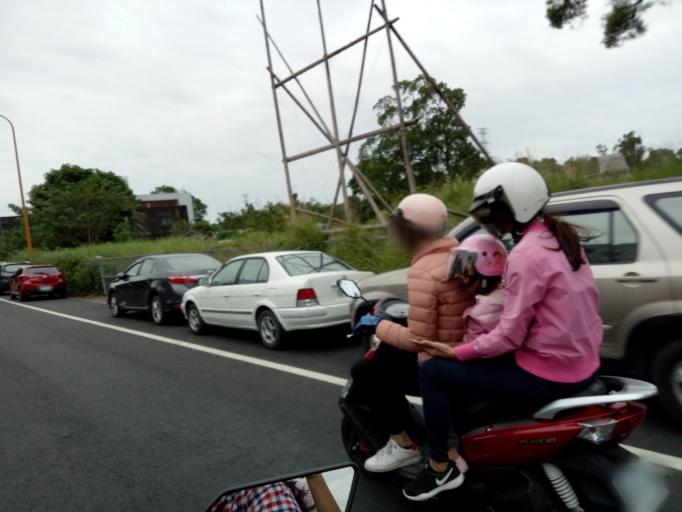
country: TW
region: Taiwan
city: Daxi
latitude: 24.8800
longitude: 121.2642
